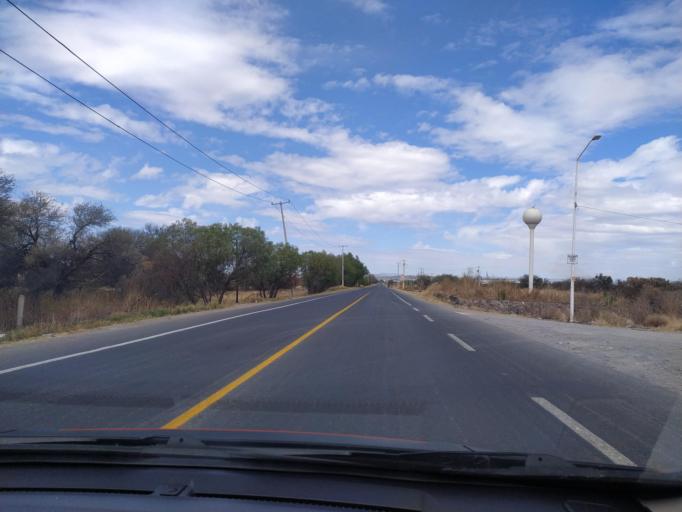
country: LA
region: Oudomxai
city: Muang La
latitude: 20.9961
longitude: 101.8338
